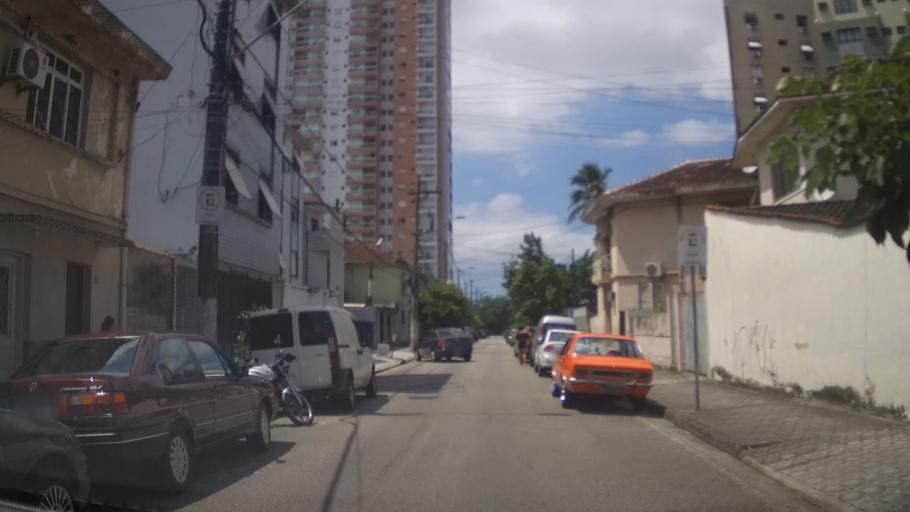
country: BR
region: Sao Paulo
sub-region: Santos
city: Santos
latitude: -23.9602
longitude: -46.3173
